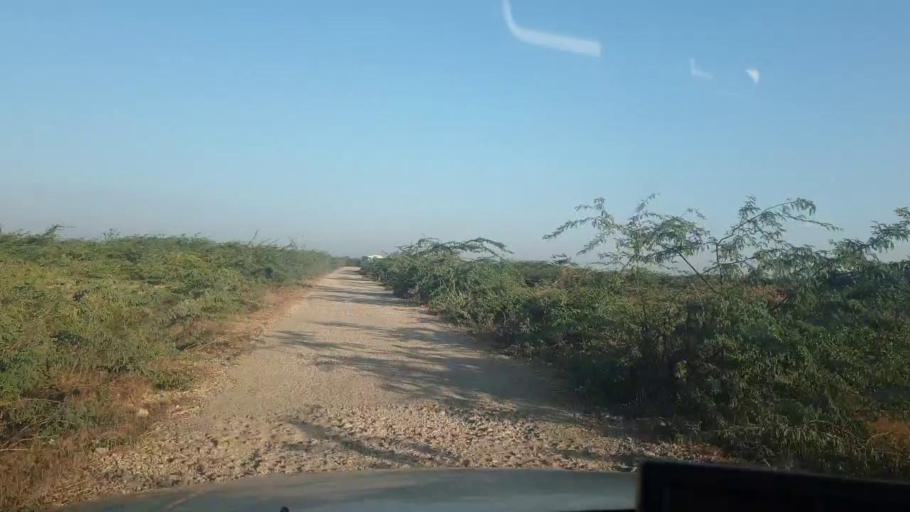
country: PK
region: Sindh
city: Thatta
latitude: 24.7091
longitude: 67.8470
